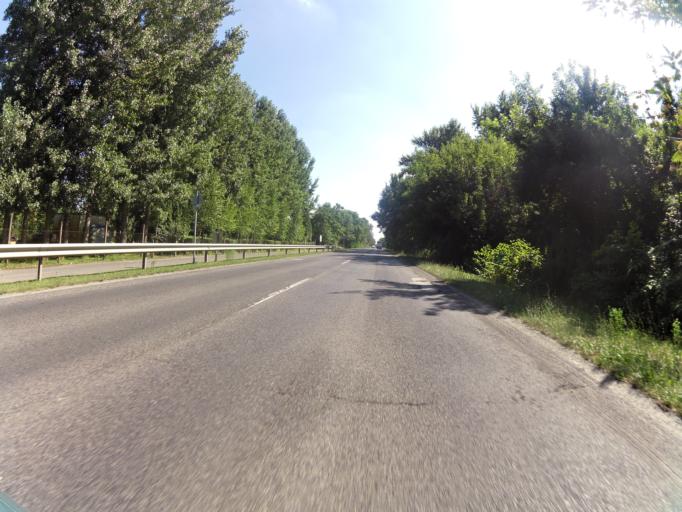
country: HU
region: Csongrad
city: Szatymaz
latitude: 46.3309
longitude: 20.0644
